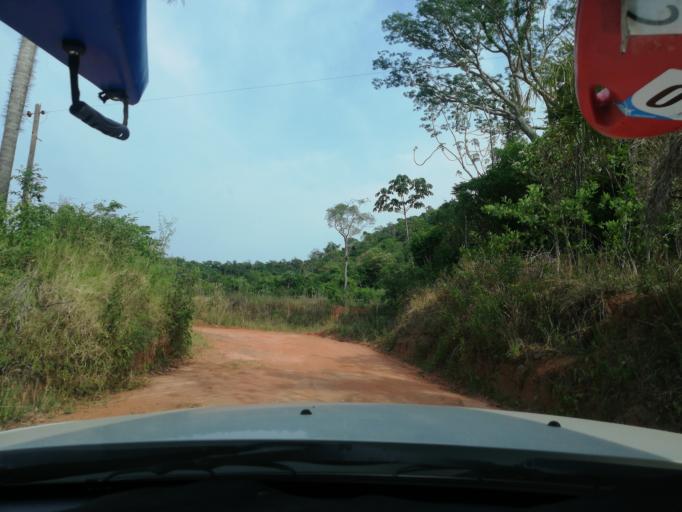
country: AR
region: Misiones
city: Santa Ana
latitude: -27.3056
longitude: -55.5838
